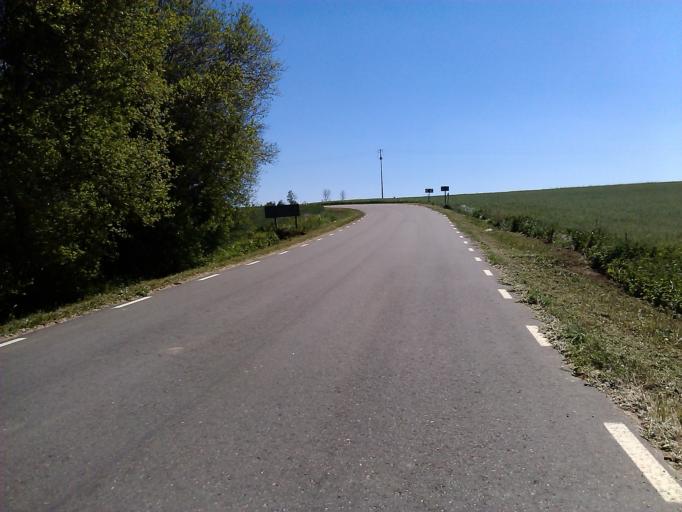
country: ES
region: Castille and Leon
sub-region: Provincia de Burgos
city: Arlanzon
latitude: 42.3555
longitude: -3.4625
